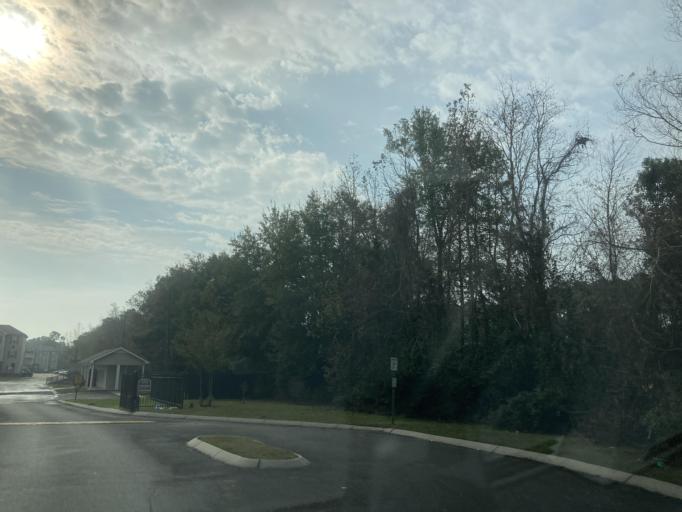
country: US
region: Mississippi
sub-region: Harrison County
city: Gulfport
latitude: 30.3704
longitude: -89.1223
